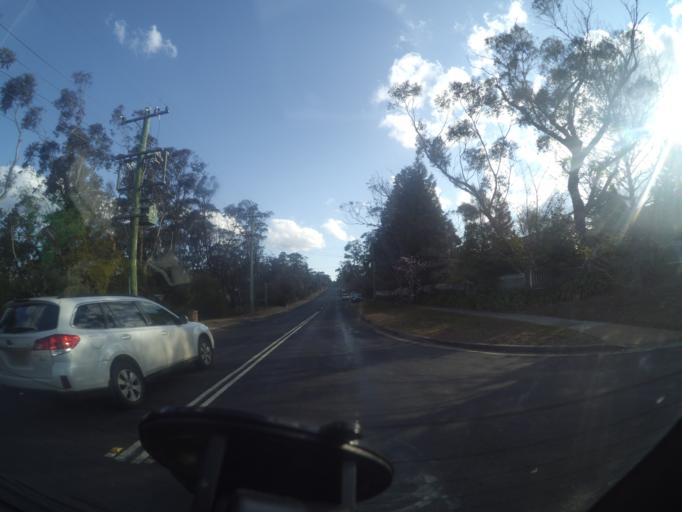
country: AU
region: New South Wales
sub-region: Blue Mountains Municipality
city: Blackheath
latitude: -33.6320
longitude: 150.3055
